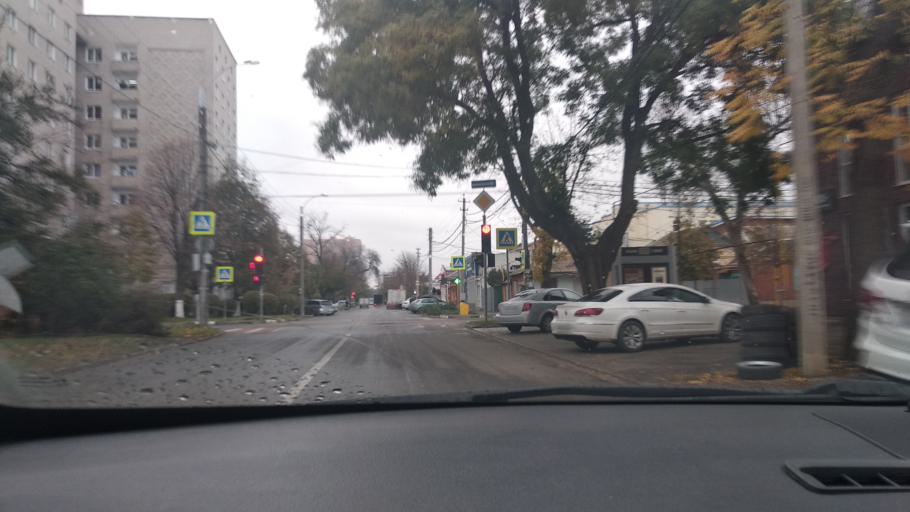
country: RU
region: Krasnodarskiy
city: Krasnodar
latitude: 45.0324
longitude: 38.9844
